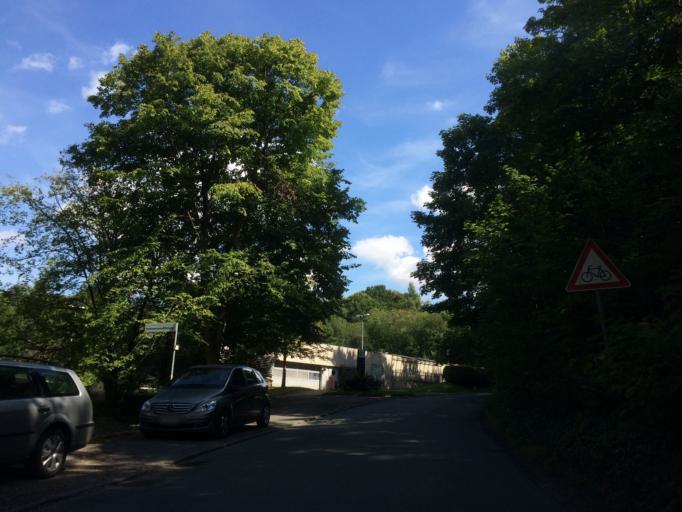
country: DE
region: Schleswig-Holstein
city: Malente
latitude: 54.1657
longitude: 10.5500
